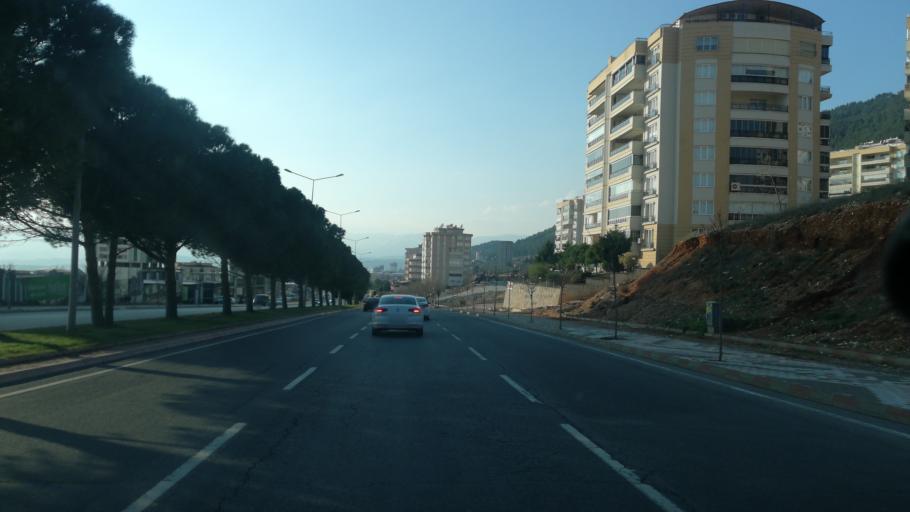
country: TR
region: Kahramanmaras
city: Kahramanmaras
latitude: 37.5966
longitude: 36.8492
